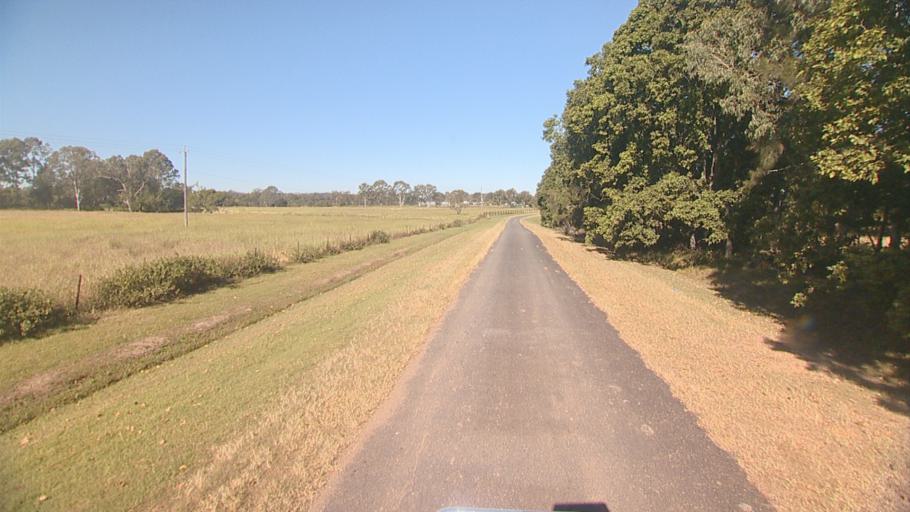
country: AU
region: Queensland
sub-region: Logan
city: Waterford West
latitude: -27.7017
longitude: 153.1288
